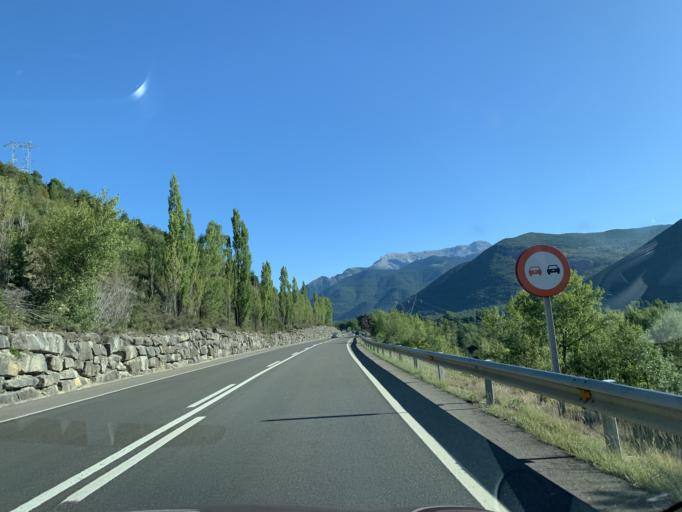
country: ES
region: Aragon
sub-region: Provincia de Huesca
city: Biescas
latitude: 42.5725
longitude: -0.3250
